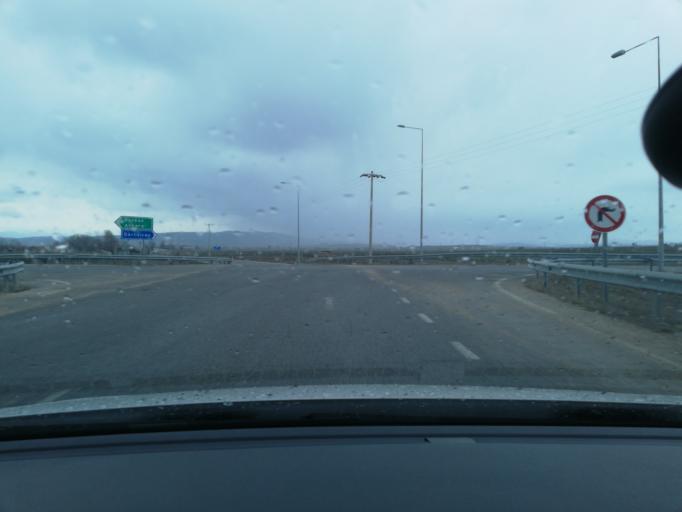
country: TR
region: Bolu
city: Dortdivan
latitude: 40.7414
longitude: 32.1172
